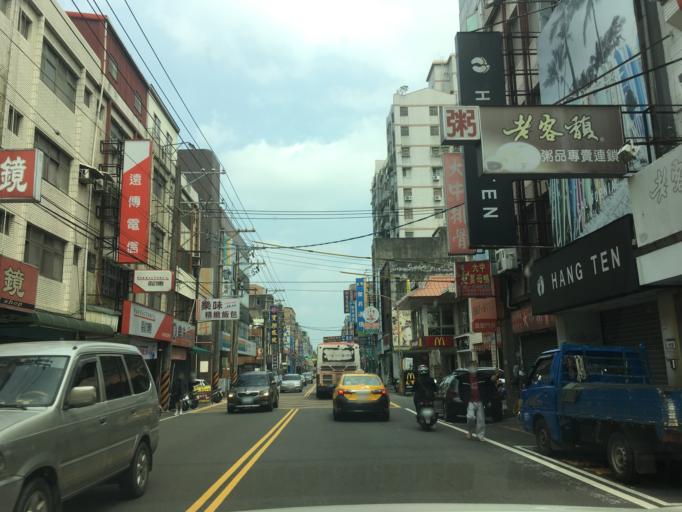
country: TW
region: Taiwan
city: Daxi
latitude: 24.8813
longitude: 121.2888
